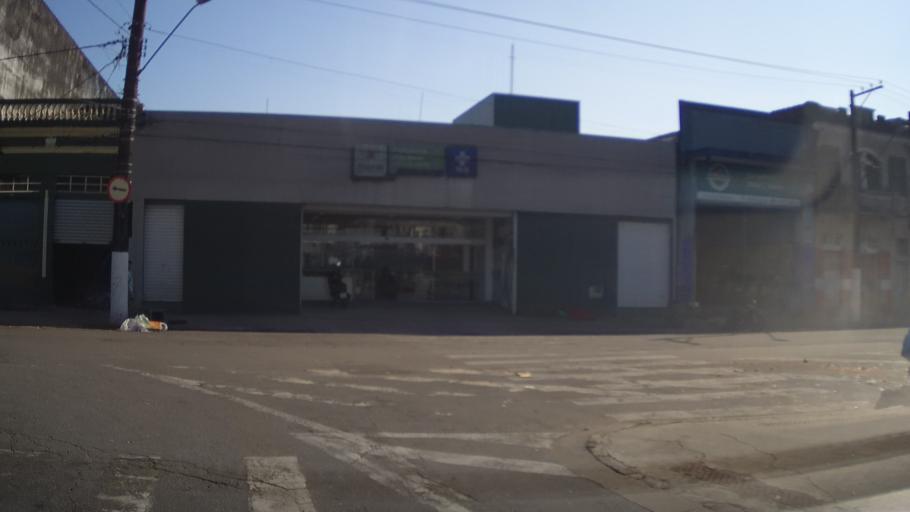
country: BR
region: Sao Paulo
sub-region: Santos
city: Santos
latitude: -23.9400
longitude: -46.3180
